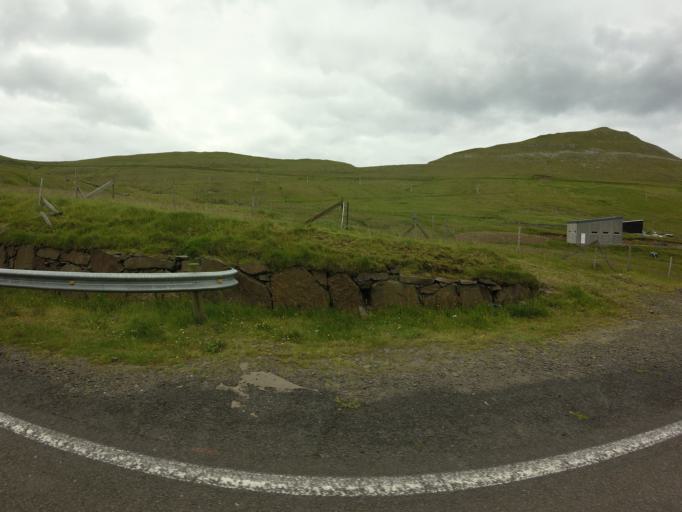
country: FO
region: Suduroy
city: Vagur
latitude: 61.4381
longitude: -6.7698
